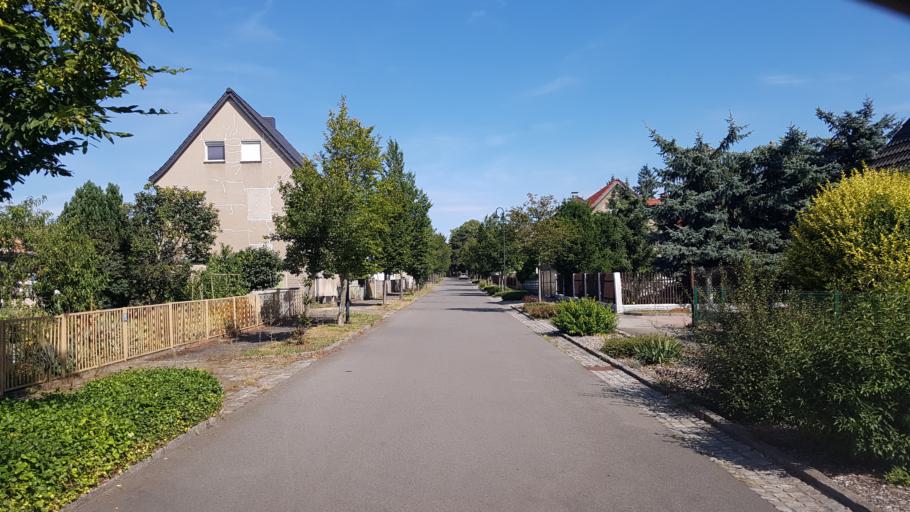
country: DE
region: Brandenburg
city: Plessa
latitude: 51.4681
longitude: 13.6205
